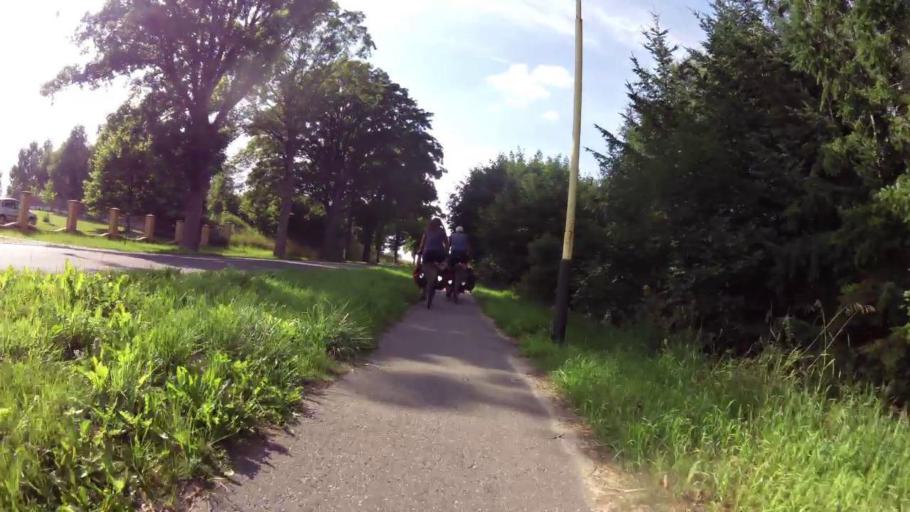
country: PL
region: West Pomeranian Voivodeship
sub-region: Powiat lobeski
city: Wegorzyno
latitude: 53.5483
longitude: 15.5463
